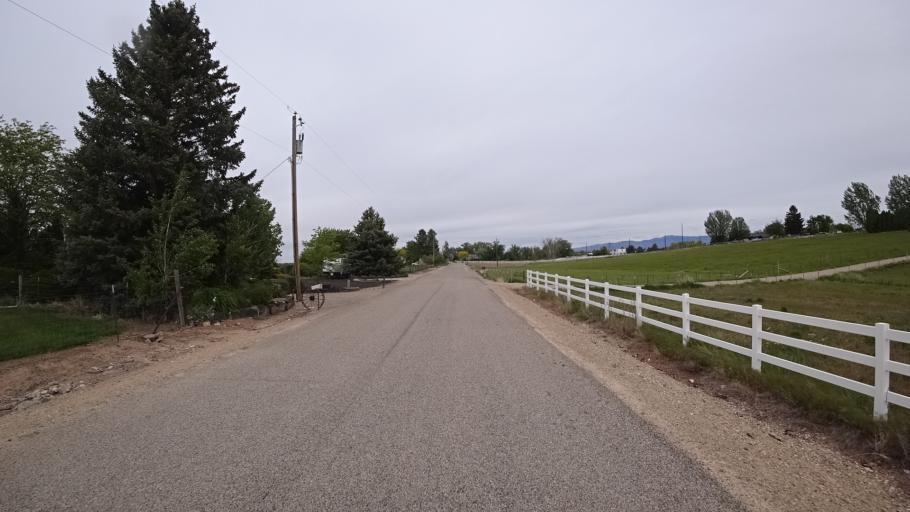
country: US
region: Idaho
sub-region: Ada County
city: Kuna
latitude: 43.5007
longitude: -116.3394
